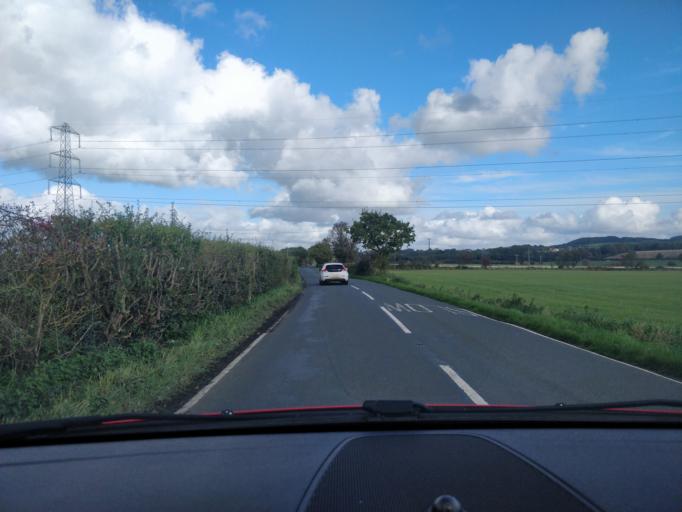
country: GB
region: England
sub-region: Lancashire
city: Parbold
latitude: 53.6073
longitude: -2.7923
